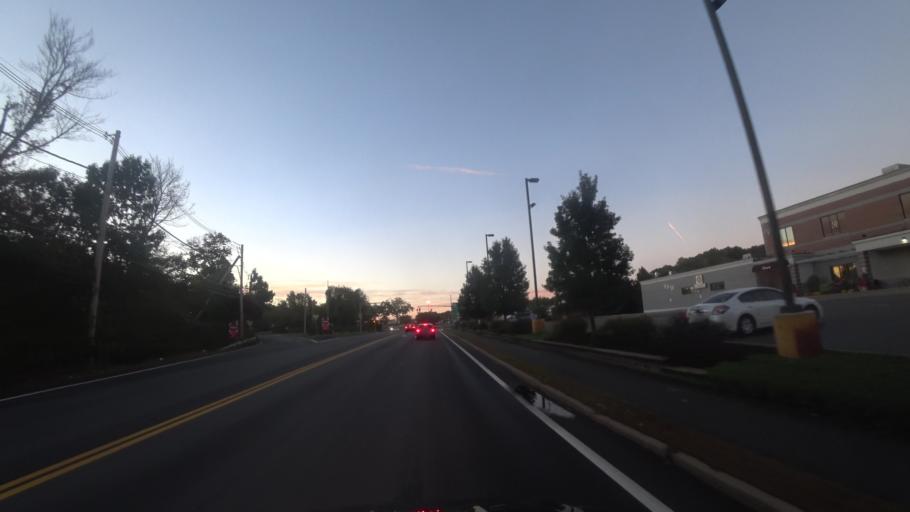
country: US
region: Massachusetts
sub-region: Essex County
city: Saugus
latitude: 42.4672
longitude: -71.0274
